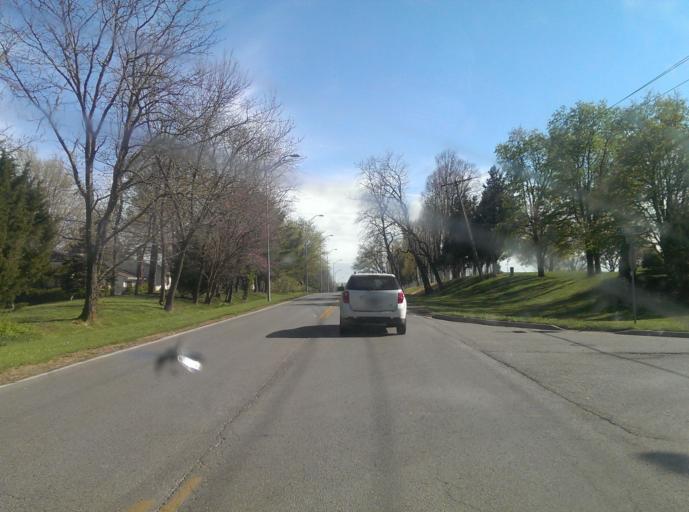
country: US
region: Missouri
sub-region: Jackson County
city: Grandview
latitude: 38.8957
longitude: -94.5949
